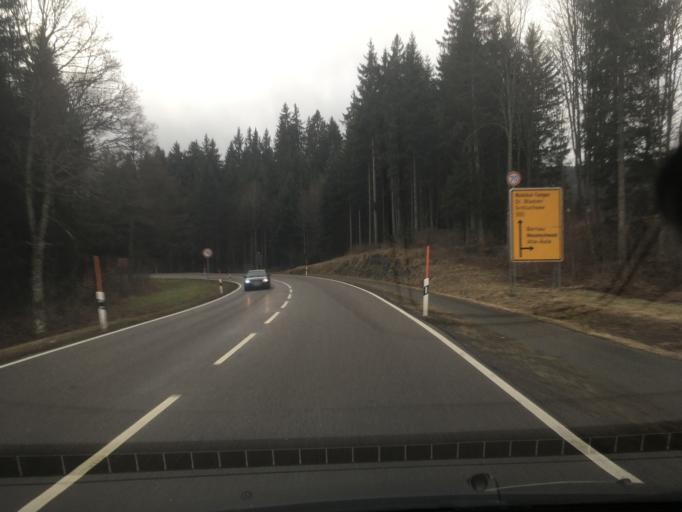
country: DE
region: Baden-Wuerttemberg
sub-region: Freiburg Region
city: Schluchsee
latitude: 47.8386
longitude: 8.1287
